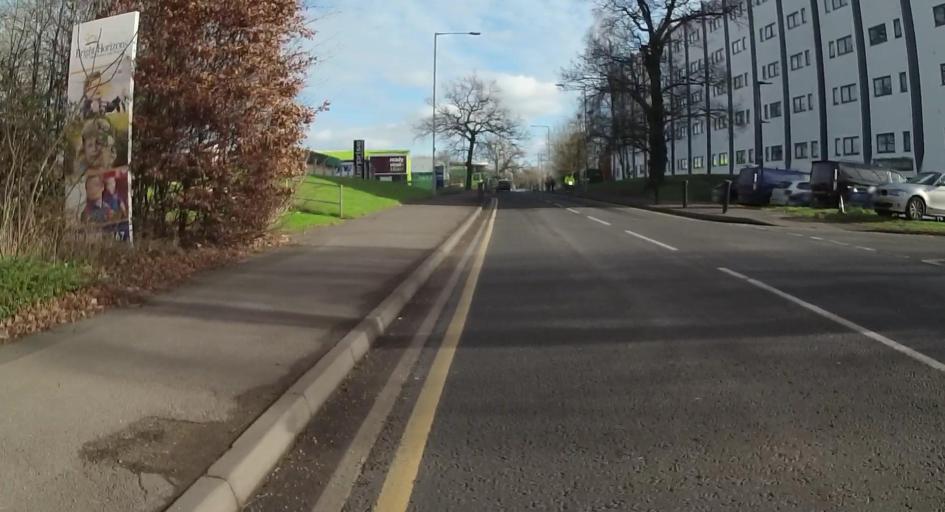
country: GB
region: England
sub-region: Wokingham
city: Wokingham
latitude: 51.4045
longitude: -0.8437
